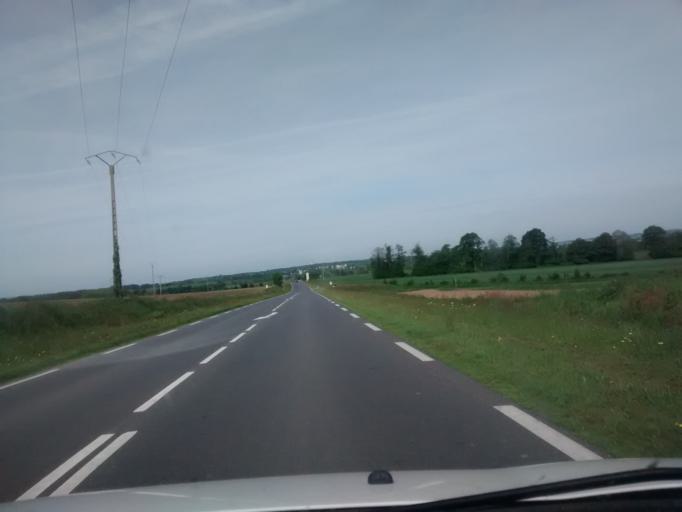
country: FR
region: Brittany
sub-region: Departement d'Ille-et-Vilaine
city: Tremblay
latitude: 48.4235
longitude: -1.4240
